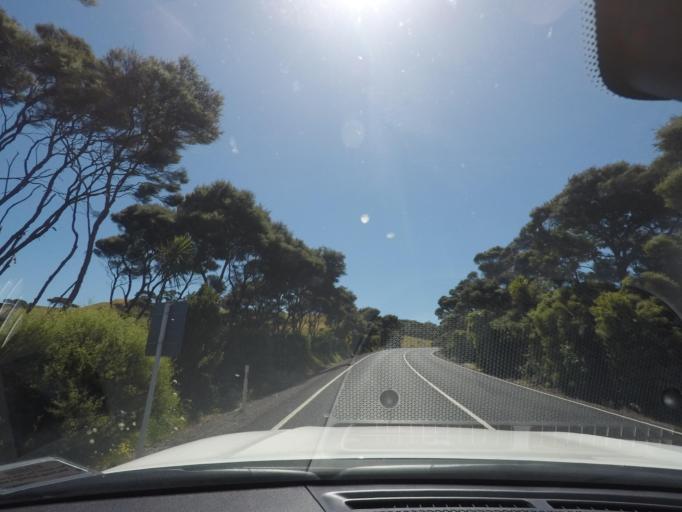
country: NZ
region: Auckland
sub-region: Auckland
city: Parakai
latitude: -36.6279
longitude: 174.3633
